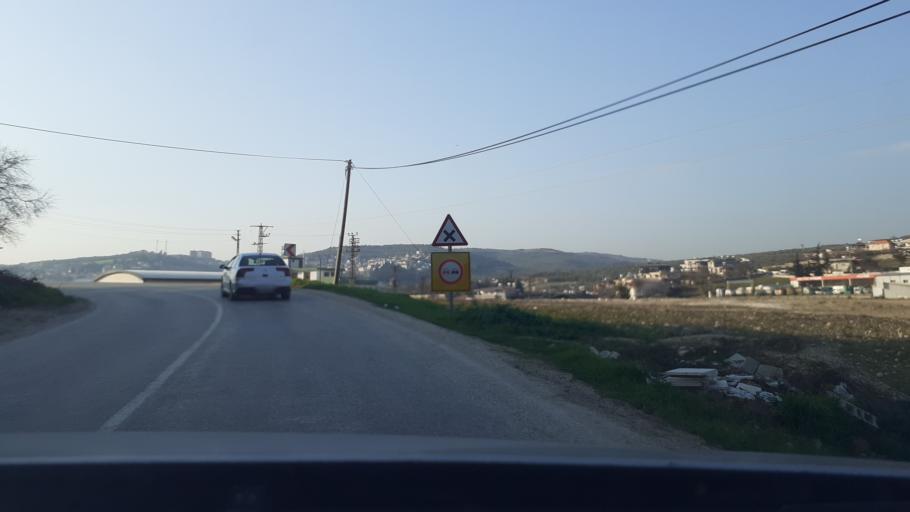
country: TR
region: Hatay
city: Fatikli
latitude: 36.1114
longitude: 36.2648
